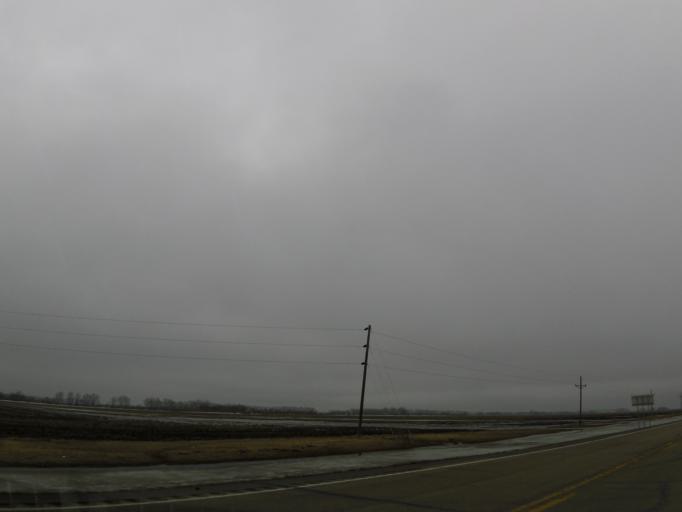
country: US
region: North Dakota
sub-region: Walsh County
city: Grafton
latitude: 48.5719
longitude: -97.4468
